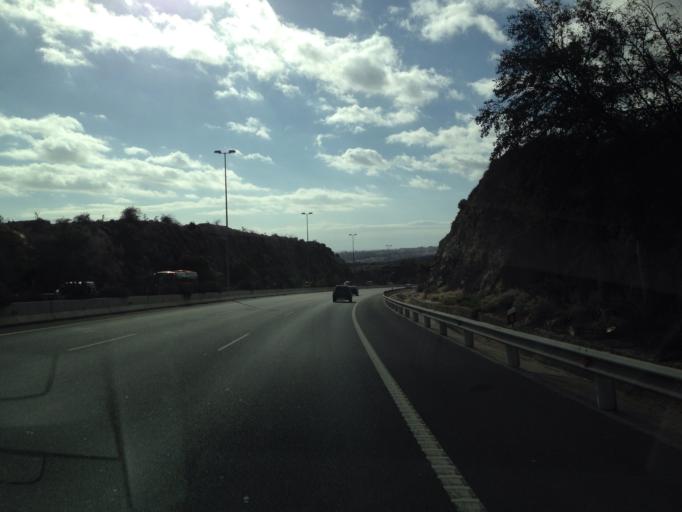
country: ES
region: Canary Islands
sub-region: Provincia de Las Palmas
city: Playa del Ingles
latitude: 27.7764
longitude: -15.5462
